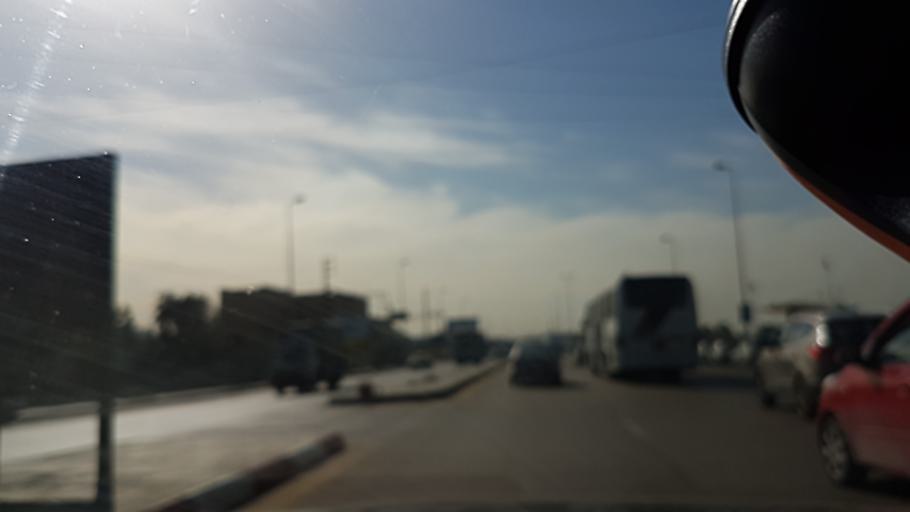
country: LB
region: Liban-Sud
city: Sidon
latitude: 33.5907
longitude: 35.3875
